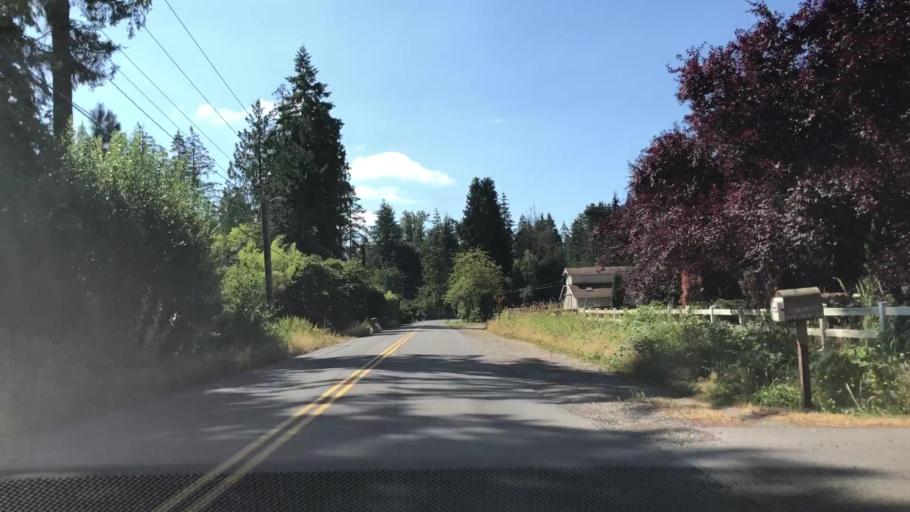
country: US
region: Washington
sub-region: King County
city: Woodinville
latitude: 47.7491
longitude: -122.1206
